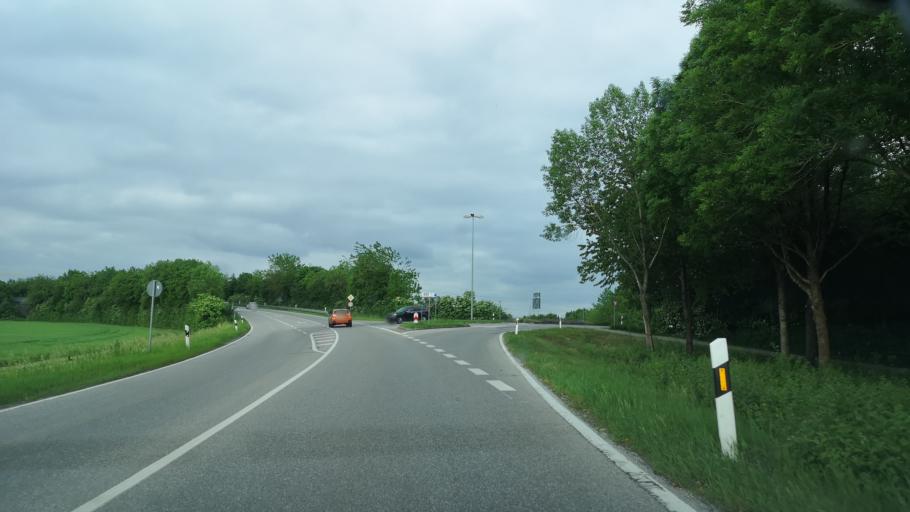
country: DE
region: Bavaria
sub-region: Upper Bavaria
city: Kirchheim bei Muenchen
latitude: 48.1639
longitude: 11.7709
